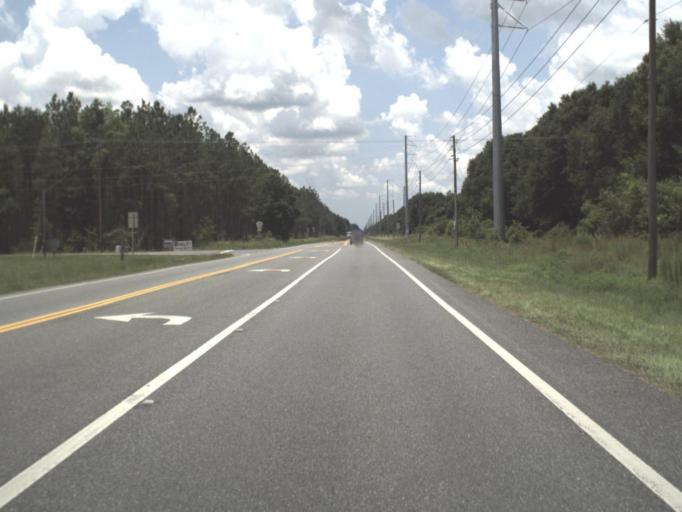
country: US
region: Florida
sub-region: Gilchrist County
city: Trenton
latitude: 29.6128
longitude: -82.8723
